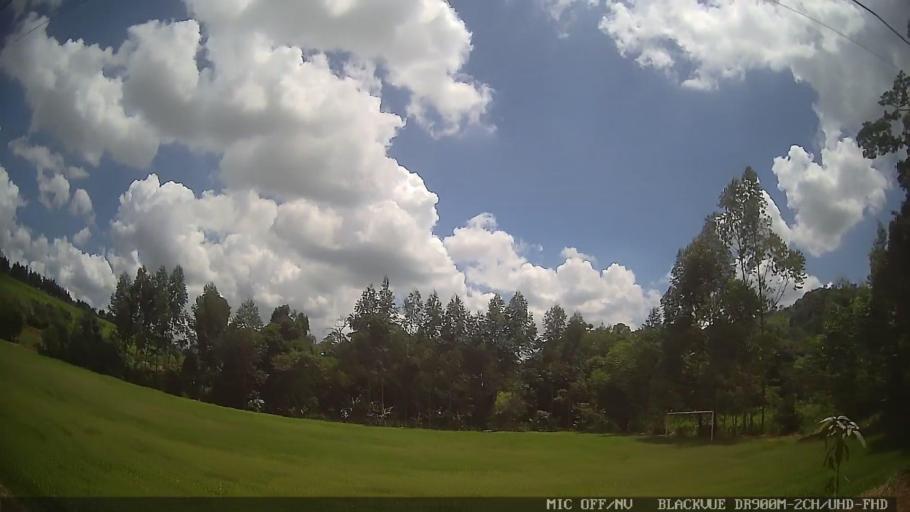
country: BR
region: Sao Paulo
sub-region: Jarinu
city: Jarinu
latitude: -23.1310
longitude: -46.6596
